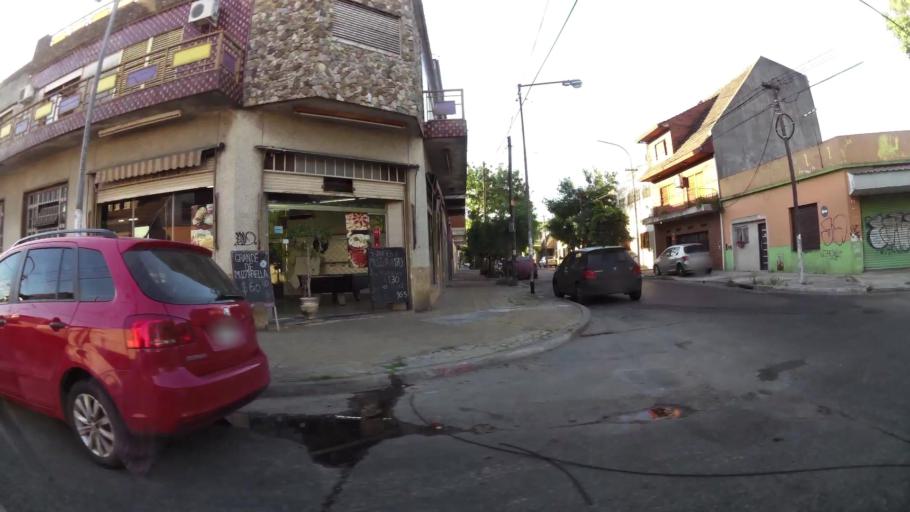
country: AR
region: Buenos Aires
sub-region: Partido de General San Martin
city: General San Martin
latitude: -34.5707
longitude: -58.5498
